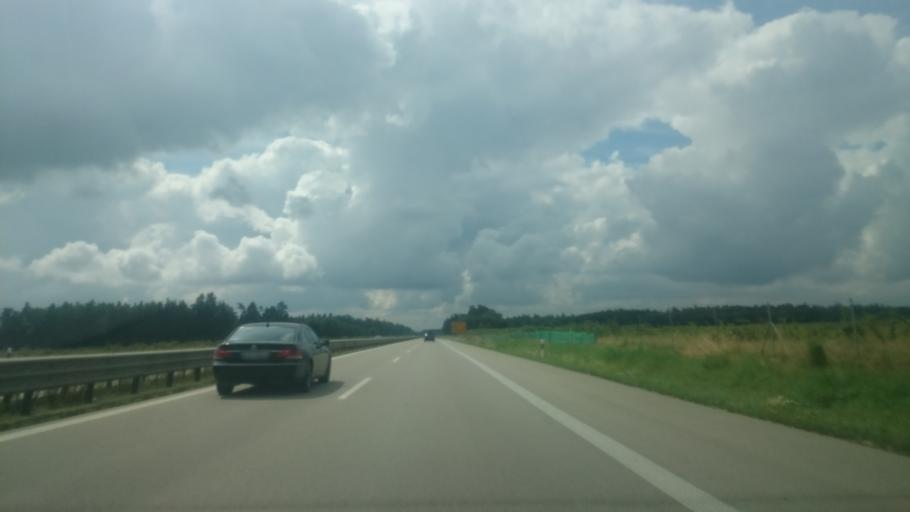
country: DE
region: Bavaria
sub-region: Upper Bavaria
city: Hurlach
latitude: 48.1078
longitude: 10.8359
